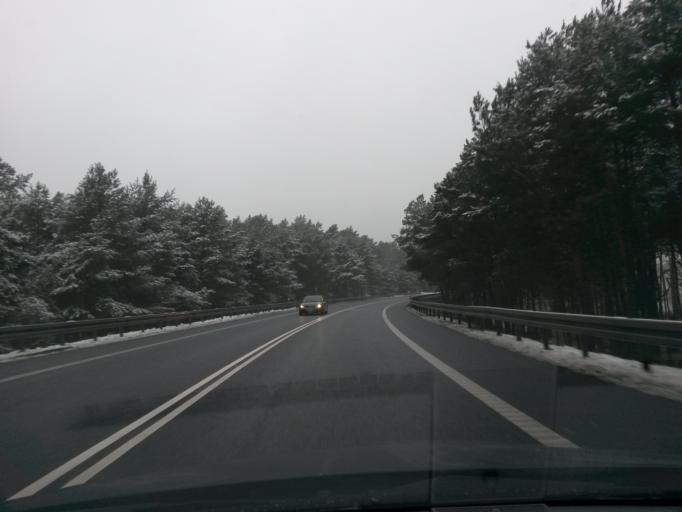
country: PL
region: Kujawsko-Pomorskie
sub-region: Powiat torunski
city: Zlawies Wielka
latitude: 53.0524
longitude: 18.3136
